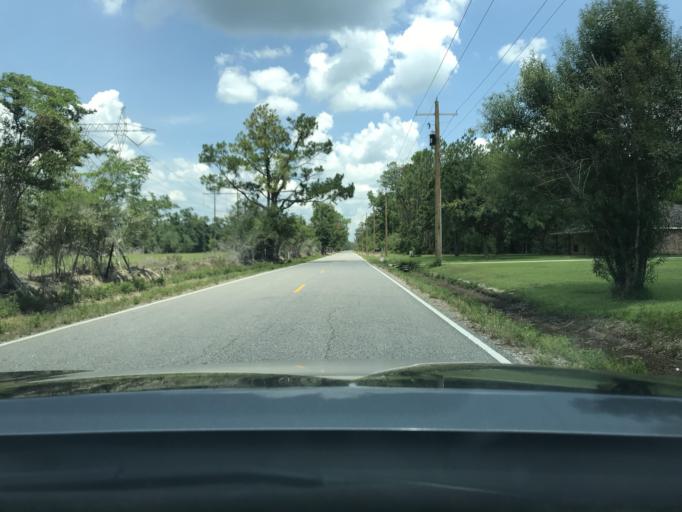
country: US
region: Louisiana
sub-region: Calcasieu Parish
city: Moss Bluff
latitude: 30.3300
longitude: -93.1647
